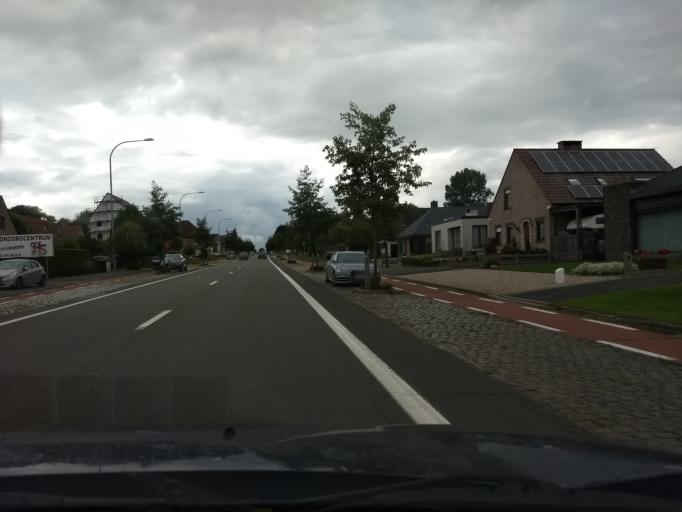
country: BE
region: Flanders
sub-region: Provincie Oost-Vlaanderen
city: Perre
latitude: 50.8964
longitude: 3.8475
